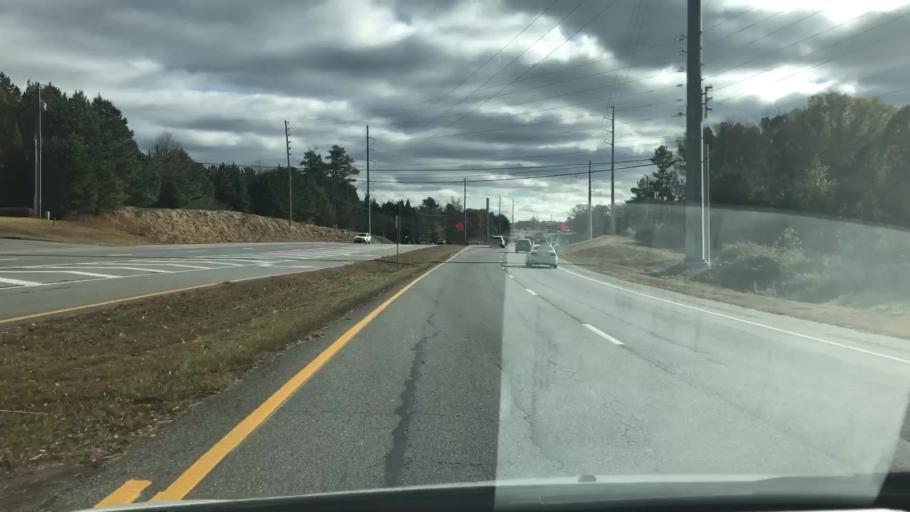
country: US
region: Georgia
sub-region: Forsyth County
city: Cumming
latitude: 34.1317
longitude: -84.1723
